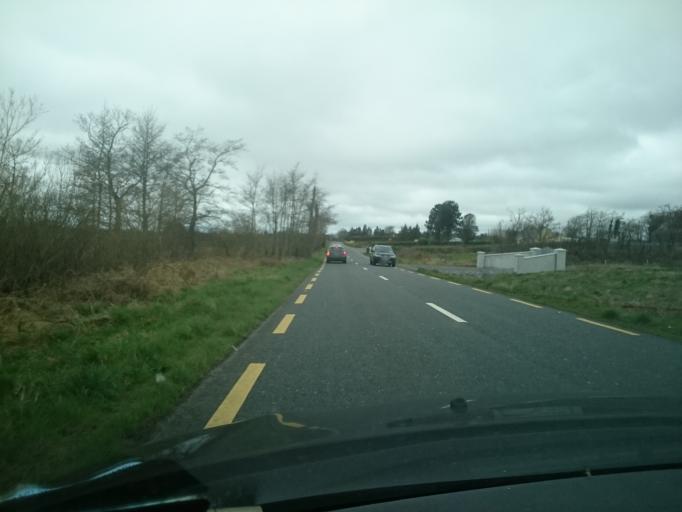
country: IE
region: Connaught
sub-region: Maigh Eo
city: Ballyhaunis
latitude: 53.7411
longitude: -8.8329
